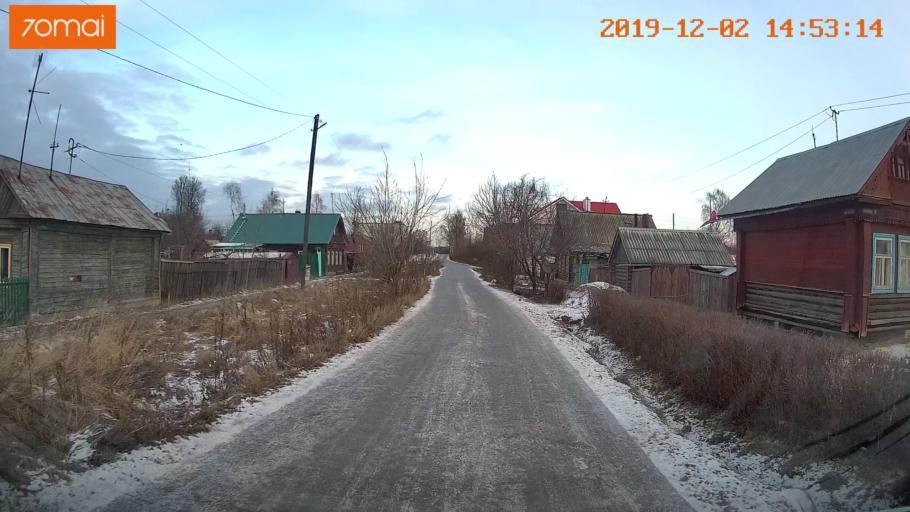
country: RU
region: Ivanovo
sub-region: Gorod Ivanovo
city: Ivanovo
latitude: 56.9751
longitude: 41.0136
